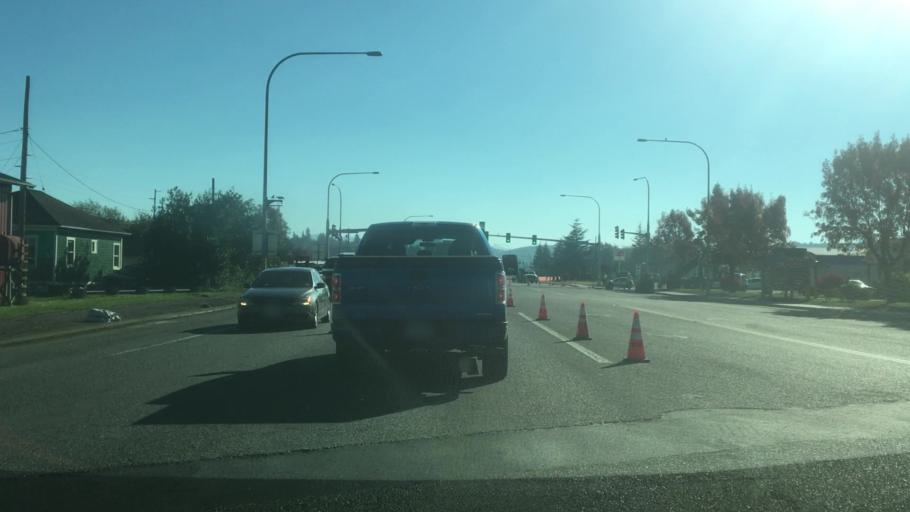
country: US
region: Washington
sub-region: Pacific County
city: Raymond
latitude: 46.6866
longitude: -123.7294
